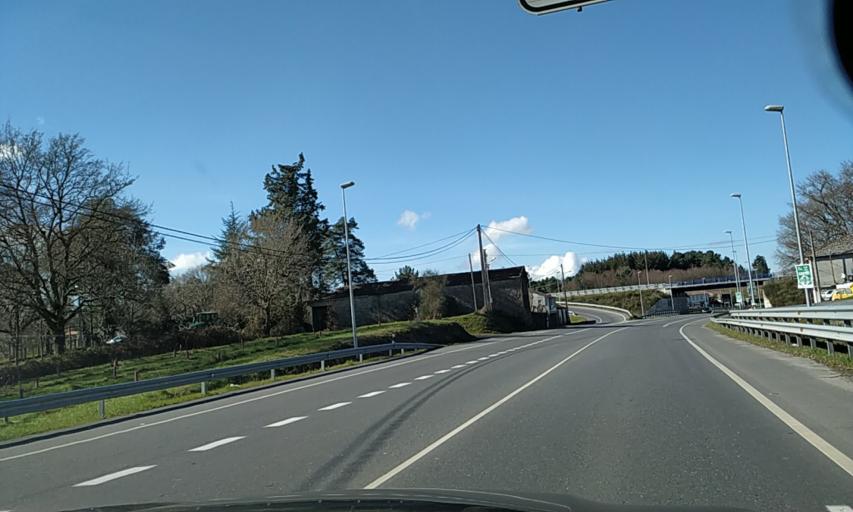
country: ES
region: Galicia
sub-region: Provincia de Pontevedra
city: Silleda
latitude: 42.7167
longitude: -8.2818
